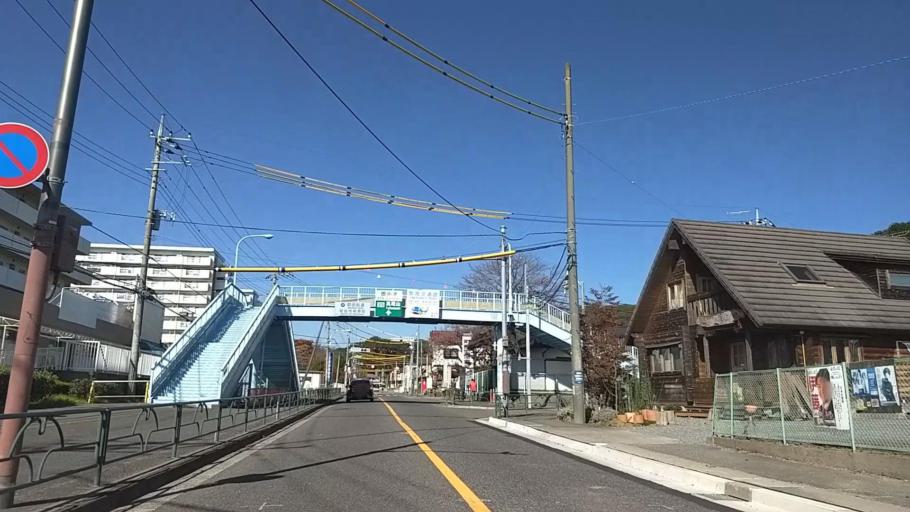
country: JP
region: Tokyo
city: Hachioji
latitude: 35.6072
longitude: 139.3017
